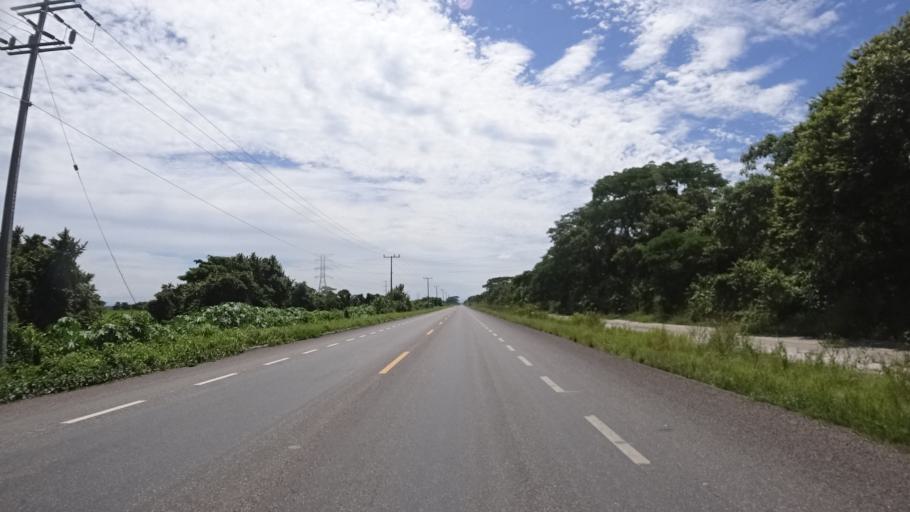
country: MX
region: Chiapas
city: Emiliano Zapata
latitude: 17.8398
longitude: -91.7951
